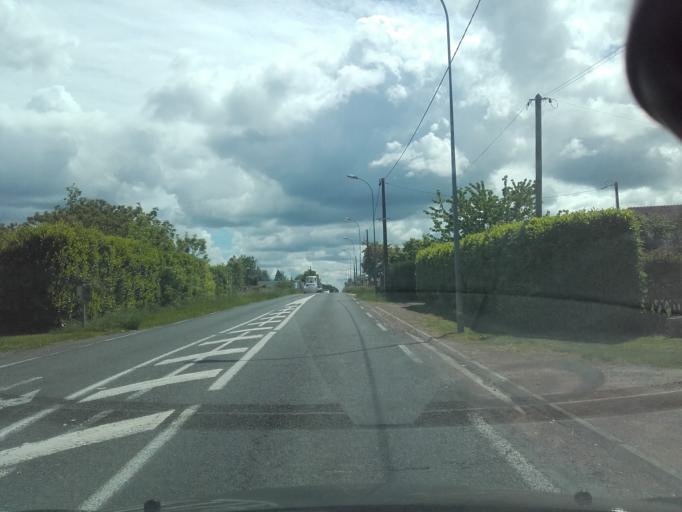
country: FR
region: Centre
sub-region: Departement d'Indre-et-Loire
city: Azay-sur-Cher
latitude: 47.3491
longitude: 0.8376
